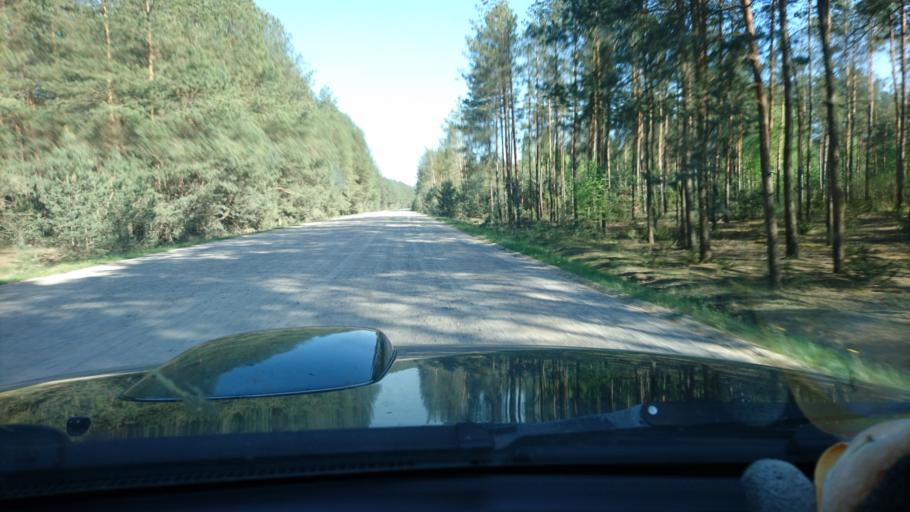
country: BY
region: Brest
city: Zhabinka
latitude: 52.3879
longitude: 24.1041
